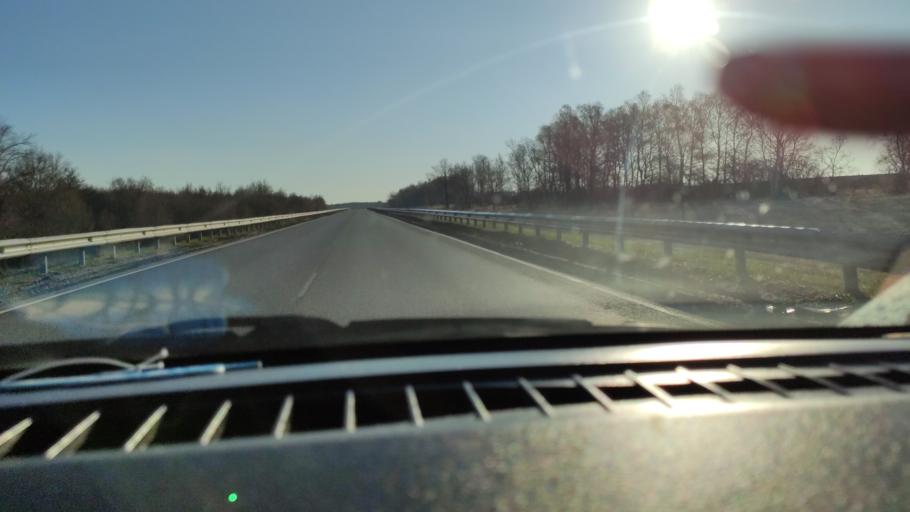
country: RU
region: Saratov
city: Balakovo
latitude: 52.0875
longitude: 47.6858
